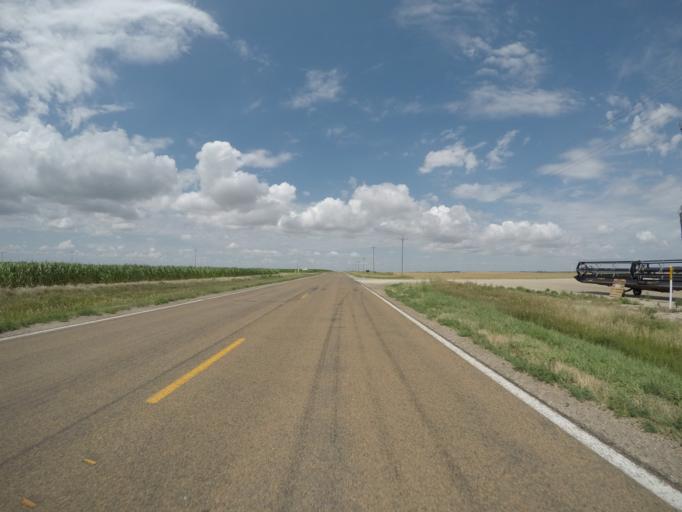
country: US
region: Kansas
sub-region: Rawlins County
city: Atwood
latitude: 39.8723
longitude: -101.0467
